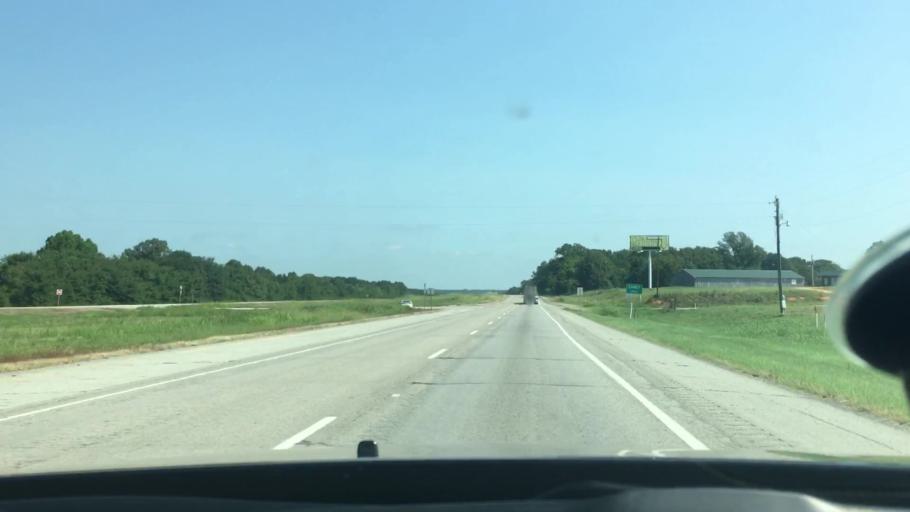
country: US
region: Oklahoma
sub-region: Atoka County
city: Atoka
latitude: 34.2286
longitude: -96.2243
